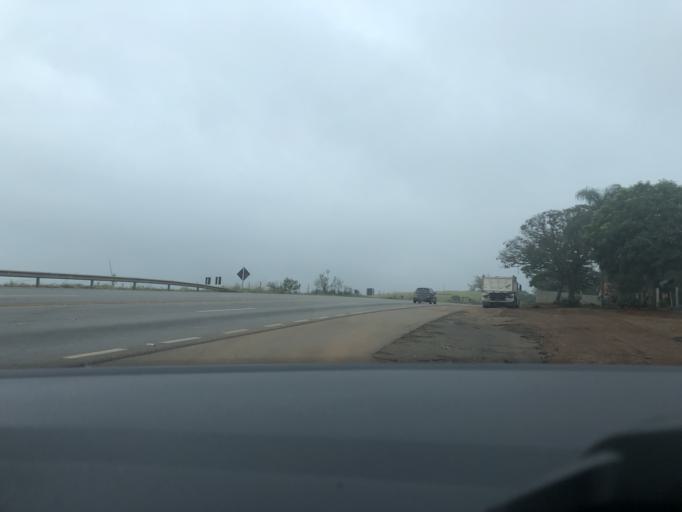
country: BR
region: Minas Gerais
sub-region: Congonhas
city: Congonhas
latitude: -20.6131
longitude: -43.9179
